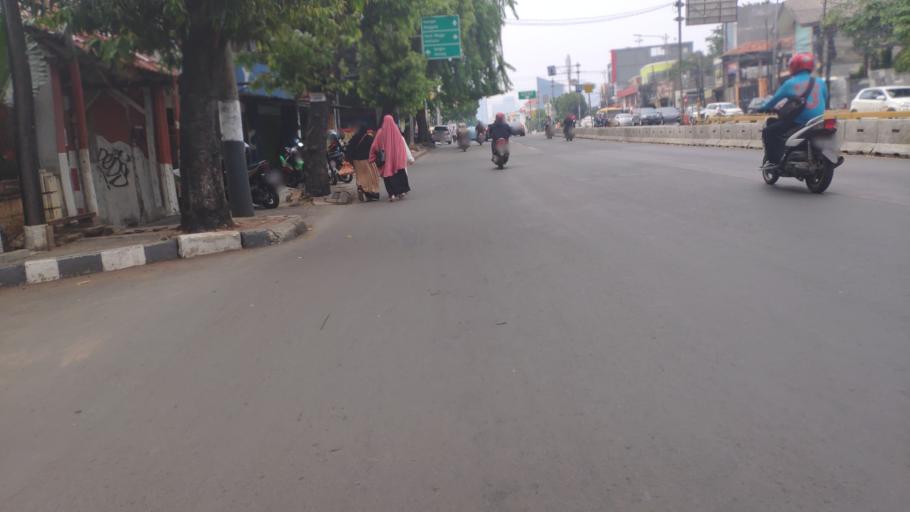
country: ID
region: Jakarta Raya
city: Jakarta
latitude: -6.2605
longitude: 106.8288
